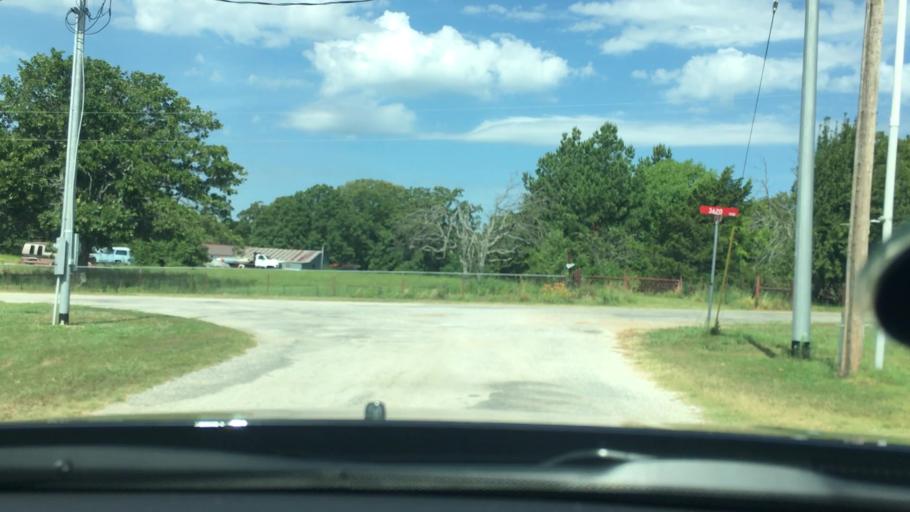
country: US
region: Oklahoma
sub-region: Pontotoc County
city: Ada
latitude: 34.7654
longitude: -96.5647
